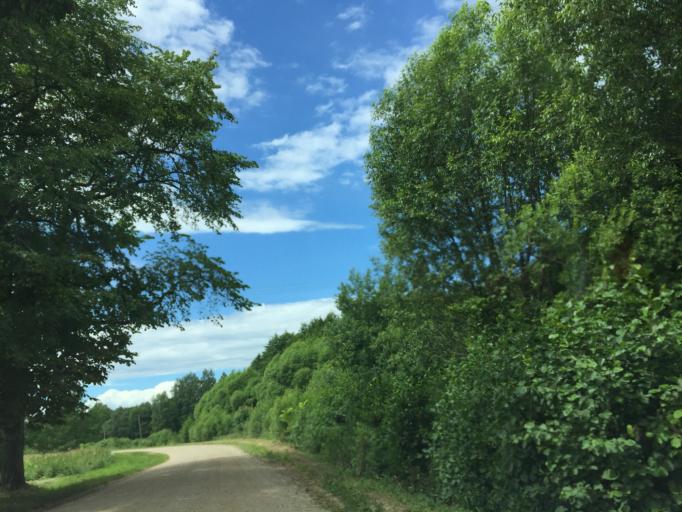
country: LV
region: Saulkrastu
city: Saulkrasti
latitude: 57.4154
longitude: 24.4126
